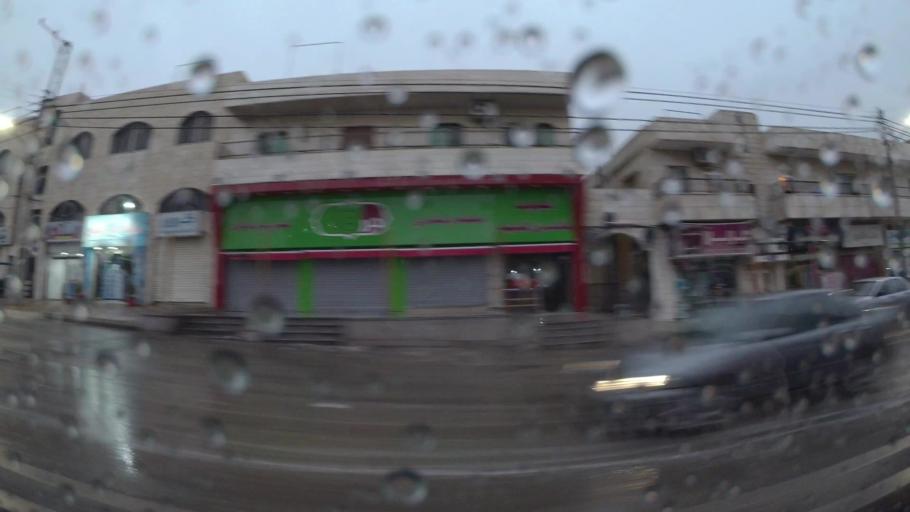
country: JO
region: Amman
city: Amman
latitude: 32.0021
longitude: 35.9666
